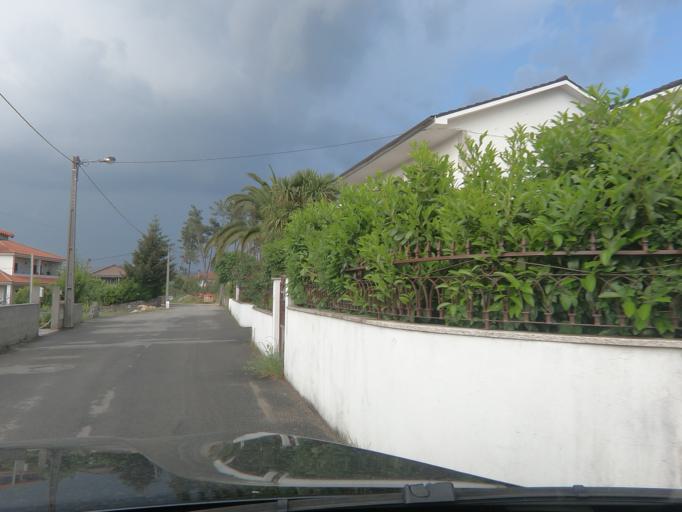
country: PT
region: Vila Real
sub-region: Vila Real
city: Vila Real
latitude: 41.3155
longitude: -7.6927
